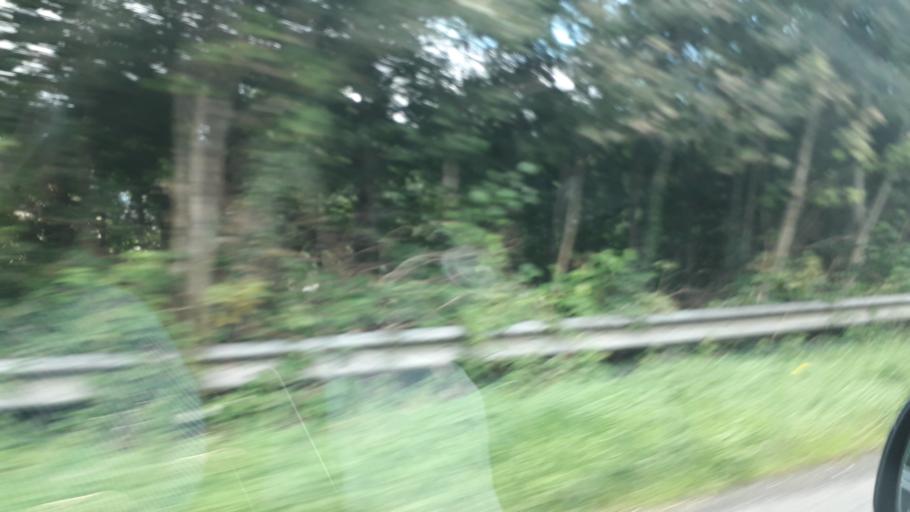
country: IE
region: Leinster
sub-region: Lu
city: Blackrock
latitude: 54.0281
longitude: -6.3501
